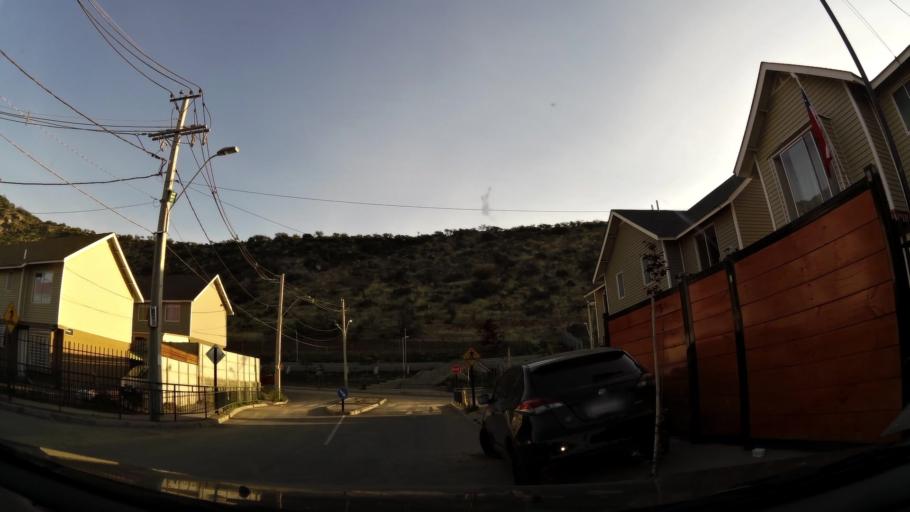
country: CL
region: Santiago Metropolitan
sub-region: Provincia de Cordillera
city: Puente Alto
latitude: -33.6022
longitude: -70.5484
